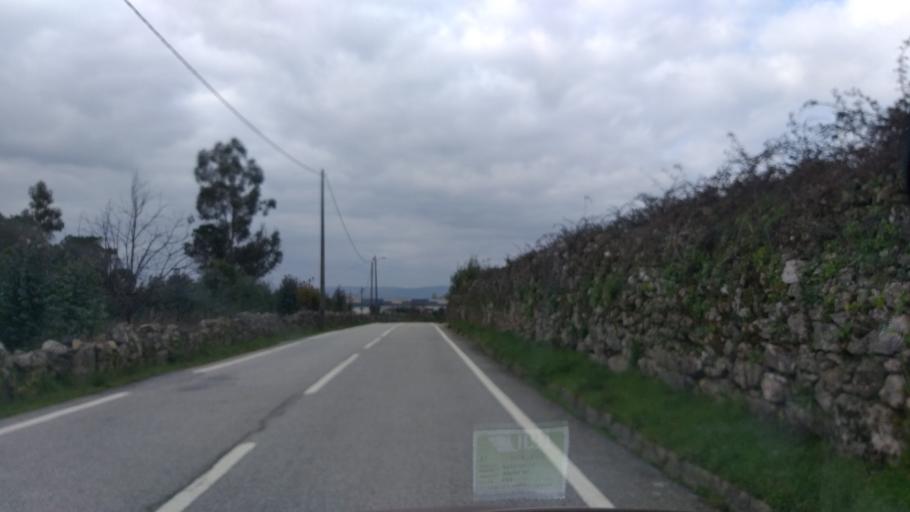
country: PT
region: Guarda
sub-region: Seia
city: Seia
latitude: 40.4809
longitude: -7.6335
